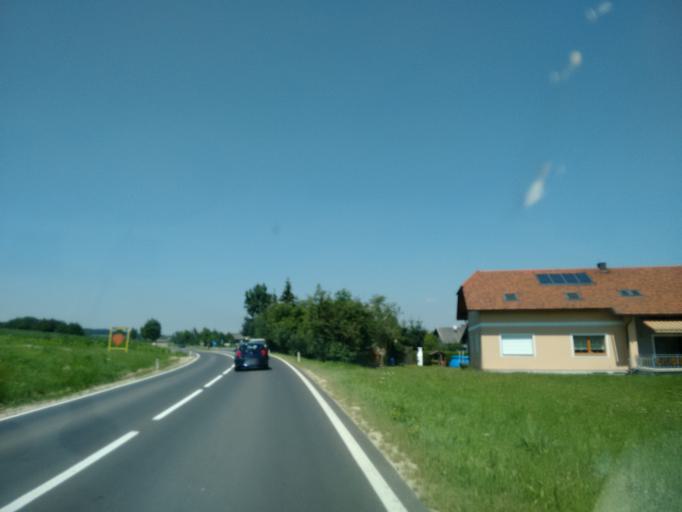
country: AT
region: Upper Austria
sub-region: Politischer Bezirk Grieskirchen
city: Bad Schallerbach
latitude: 48.2303
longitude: 13.9668
